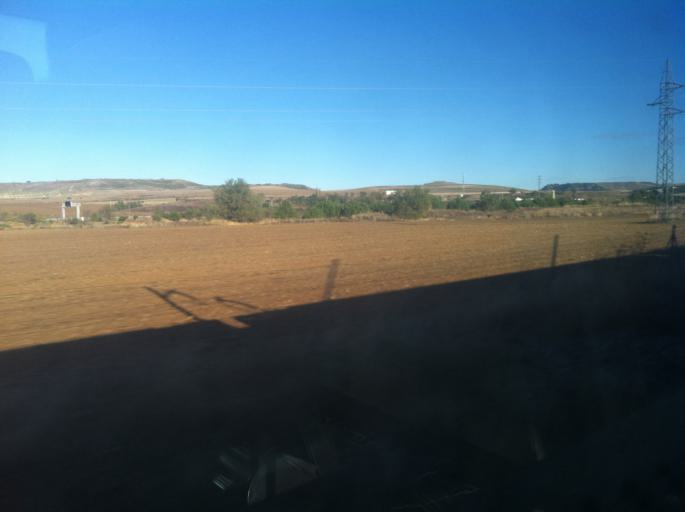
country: ES
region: Castille and Leon
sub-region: Provincia de Palencia
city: Duenas
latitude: 41.8498
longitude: -4.5542
